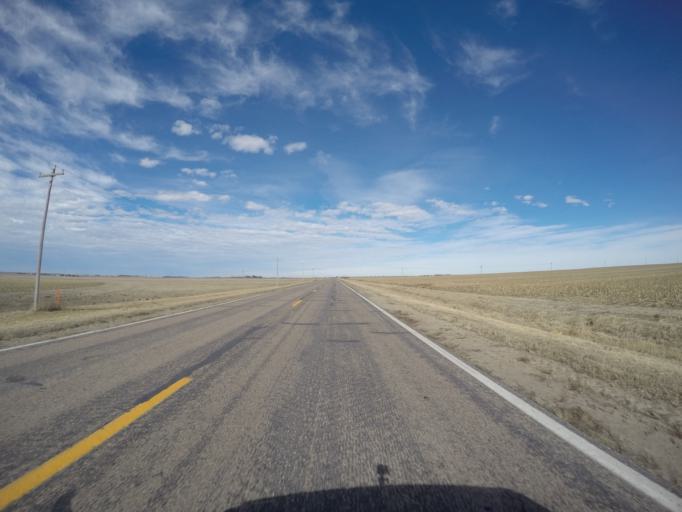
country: US
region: Nebraska
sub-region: Franklin County
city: Franklin
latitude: 40.2321
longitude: -98.9524
